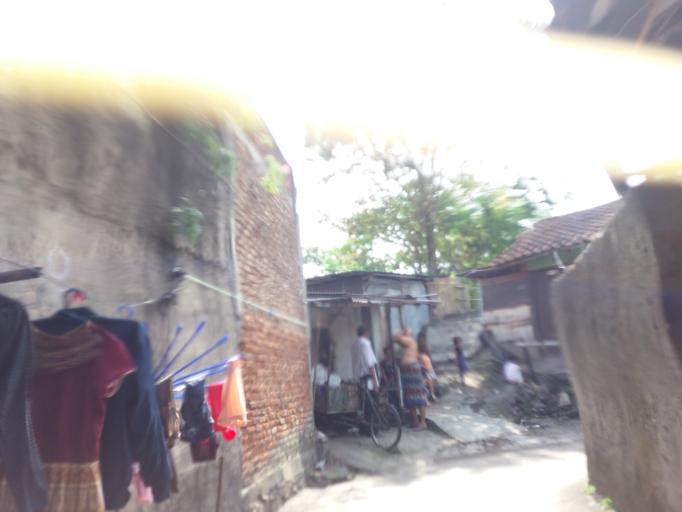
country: ID
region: West Java
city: Bandung
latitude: -6.9171
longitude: 107.6485
